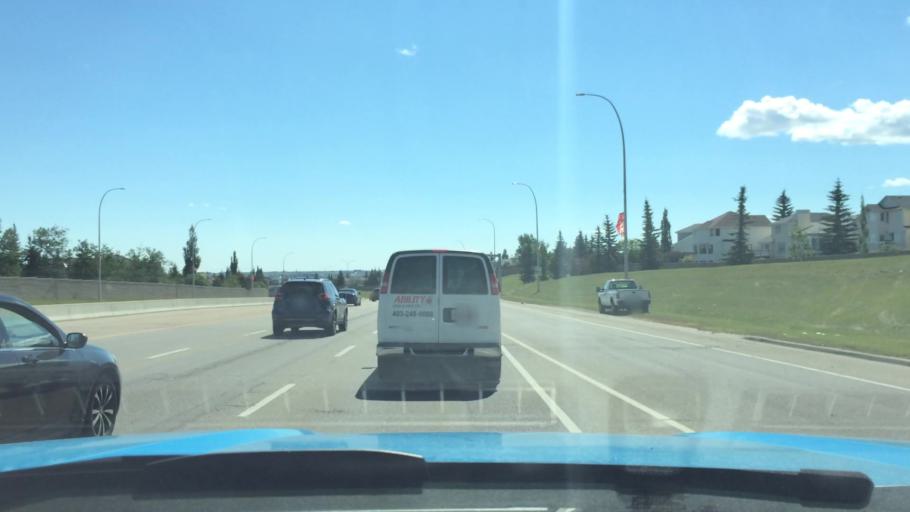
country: CA
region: Alberta
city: Calgary
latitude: 51.1429
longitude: -114.1060
